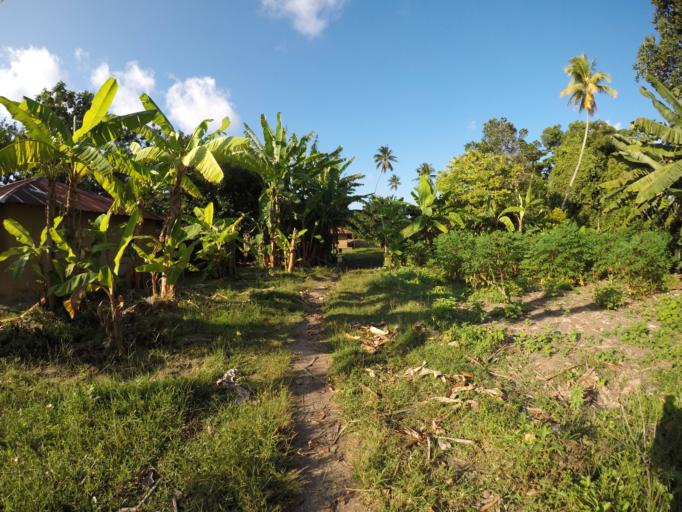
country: TZ
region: Pemba South
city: Mtambile
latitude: -5.3874
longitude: 39.7351
